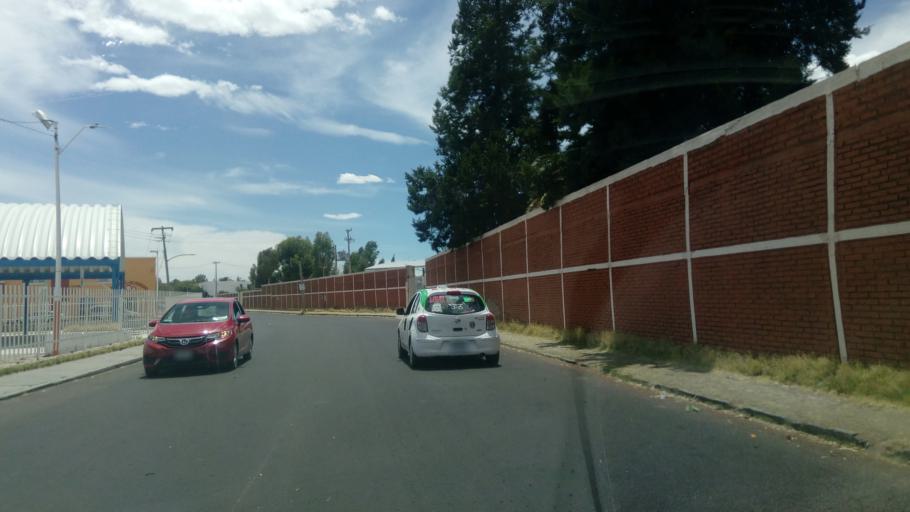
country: MX
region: Durango
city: Victoria de Durango
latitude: 24.0093
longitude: -104.6743
